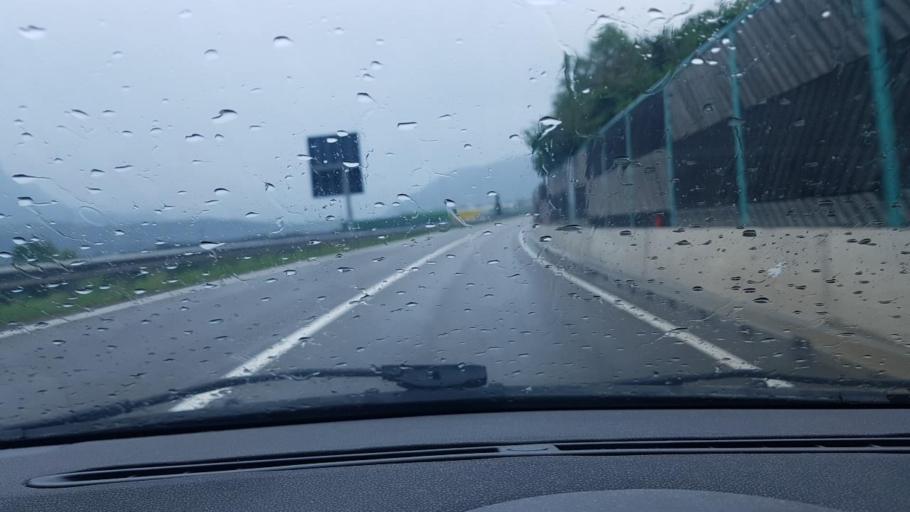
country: IT
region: Trentino-Alto Adige
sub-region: Bolzano
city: Pineta
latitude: 46.4364
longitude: 11.3452
